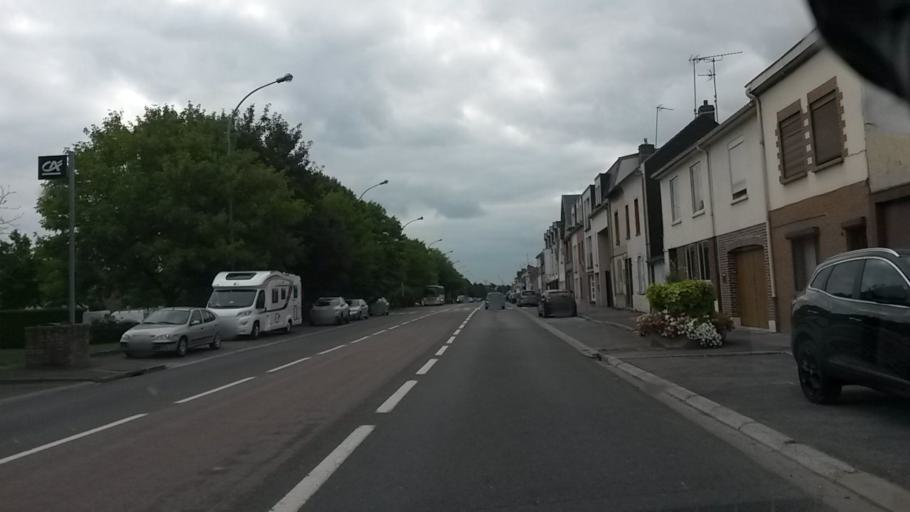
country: FR
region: Picardie
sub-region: Departement de la Somme
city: Salouel
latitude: 49.8734
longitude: 2.2470
